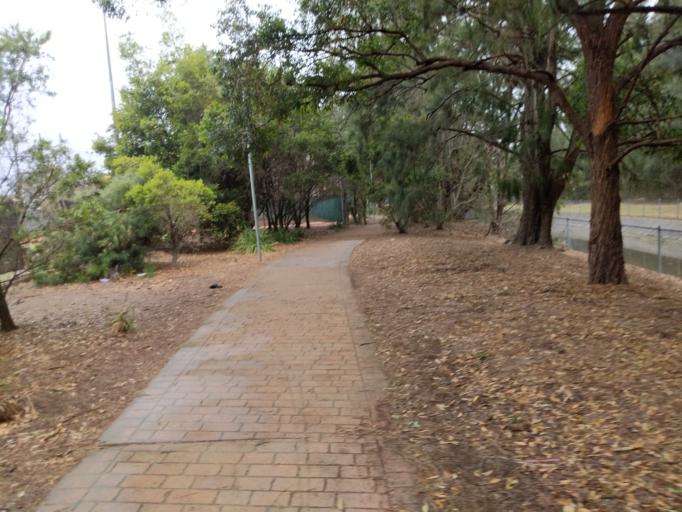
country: AU
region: New South Wales
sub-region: Ashfield
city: Croydon
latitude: -33.8663
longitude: 151.1115
